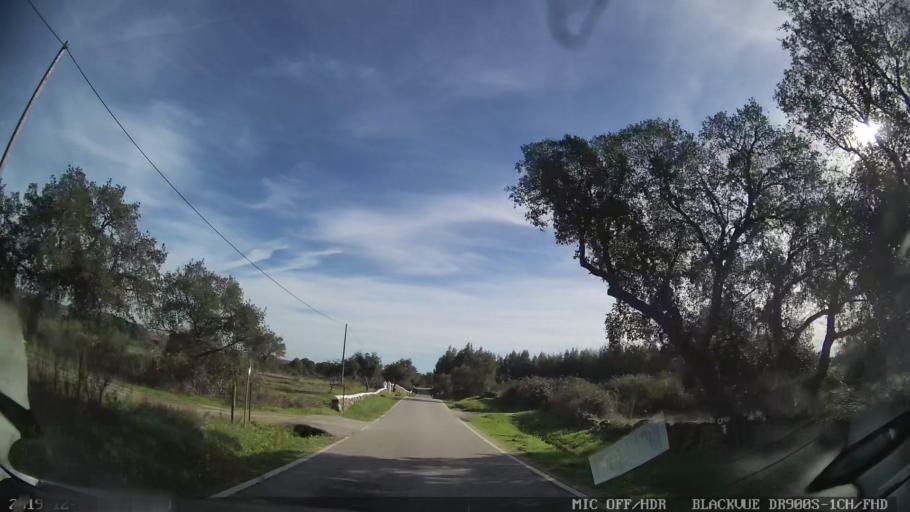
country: PT
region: Portalegre
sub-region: Nisa
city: Nisa
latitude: 39.4859
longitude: -7.7339
